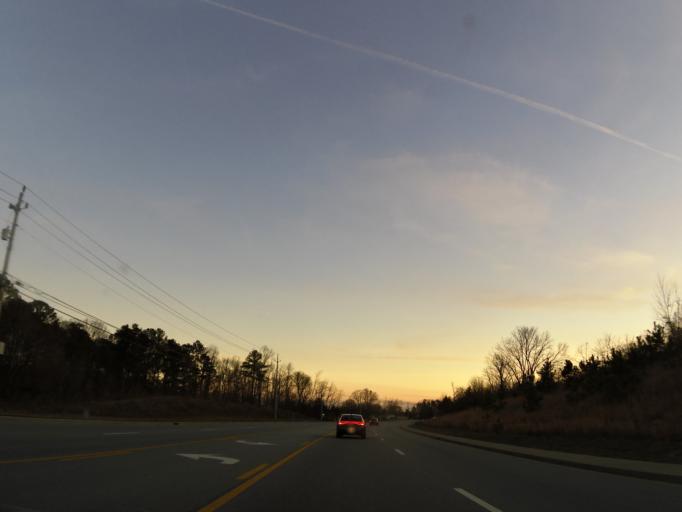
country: US
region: Tennessee
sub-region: Bradley County
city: South Cleveland
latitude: 35.1190
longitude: -84.8630
